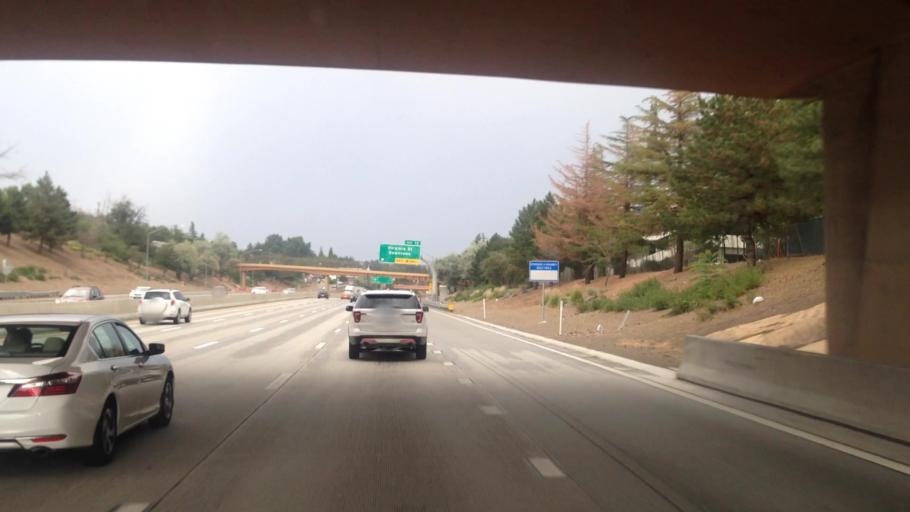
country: US
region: Nevada
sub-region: Washoe County
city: Reno
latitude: 39.5325
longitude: -119.8221
